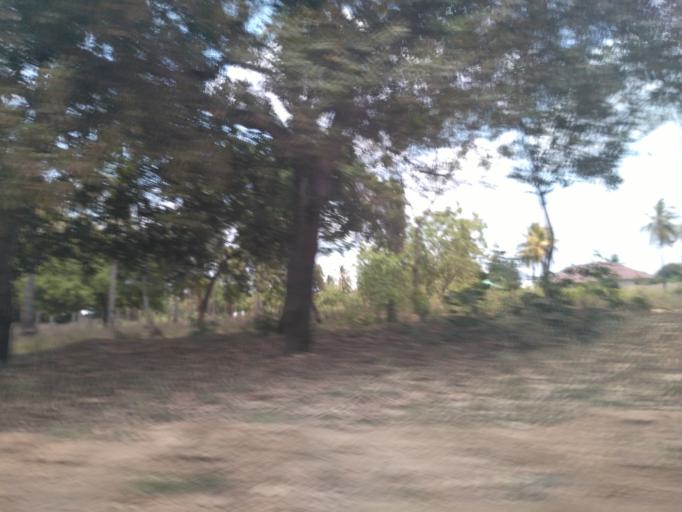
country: TZ
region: Dar es Salaam
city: Dar es Salaam
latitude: -6.8417
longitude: 39.3430
